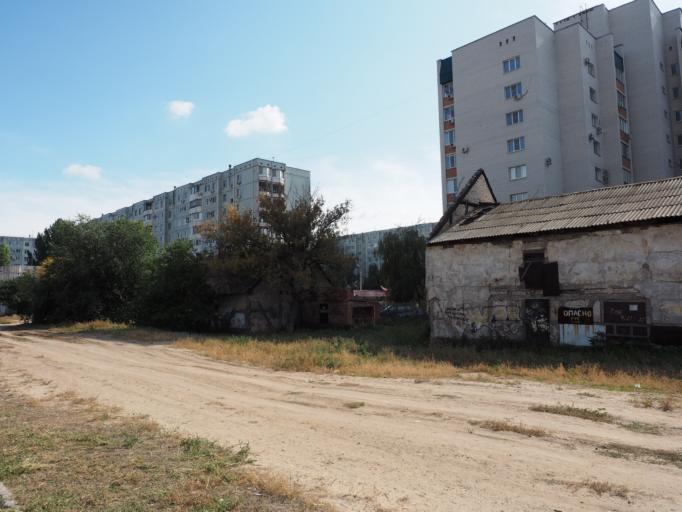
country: RU
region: Volgograd
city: Krasnoslobodsk
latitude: 48.5094
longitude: 44.5466
